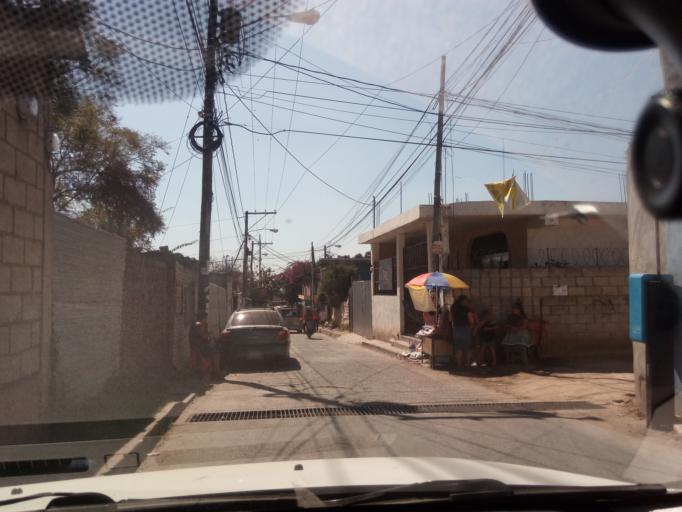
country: GT
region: Guatemala
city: Mixco
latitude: 14.6185
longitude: -90.5847
